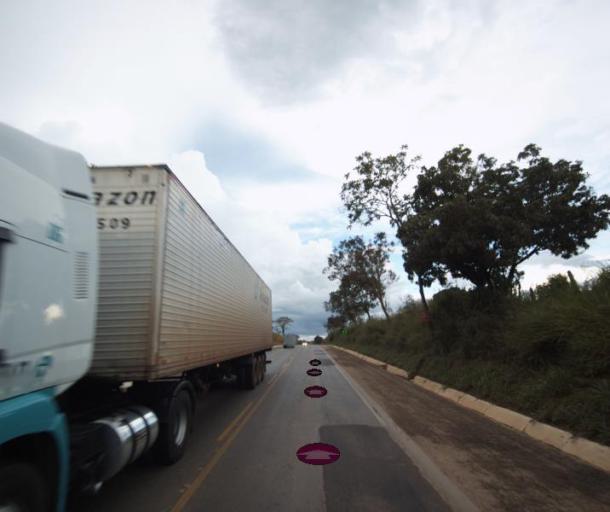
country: BR
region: Goias
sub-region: Itapaci
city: Itapaci
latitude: -14.8734
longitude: -49.3327
